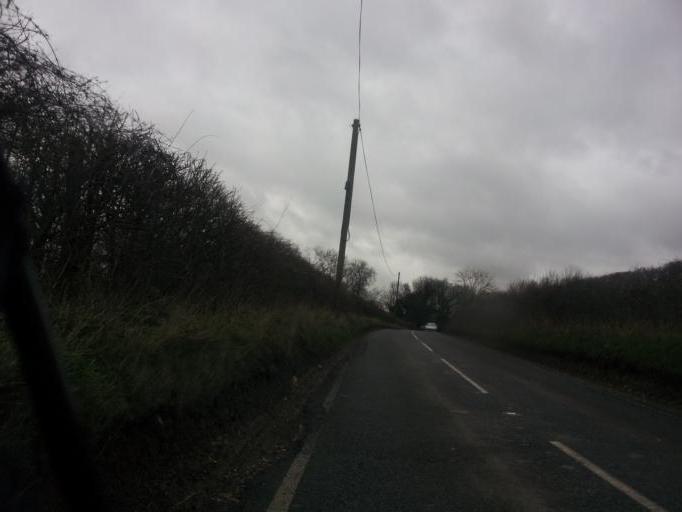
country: GB
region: England
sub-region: Kent
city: Boxley
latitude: 51.3113
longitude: 0.5487
